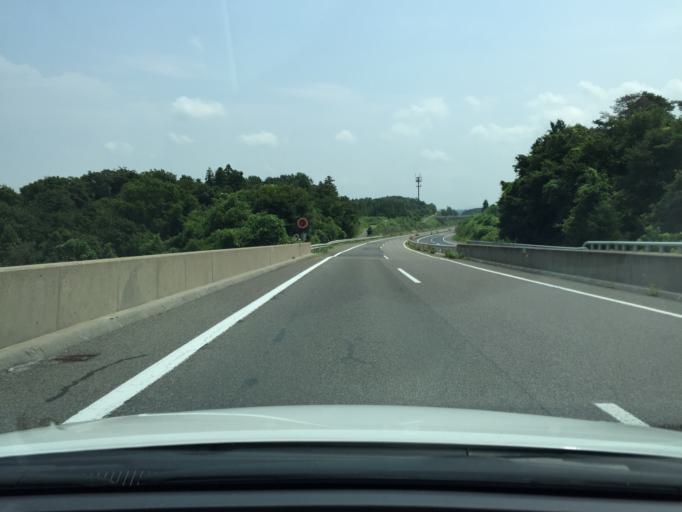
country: JP
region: Fukushima
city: Koriyama
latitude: 37.4510
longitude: 140.4098
